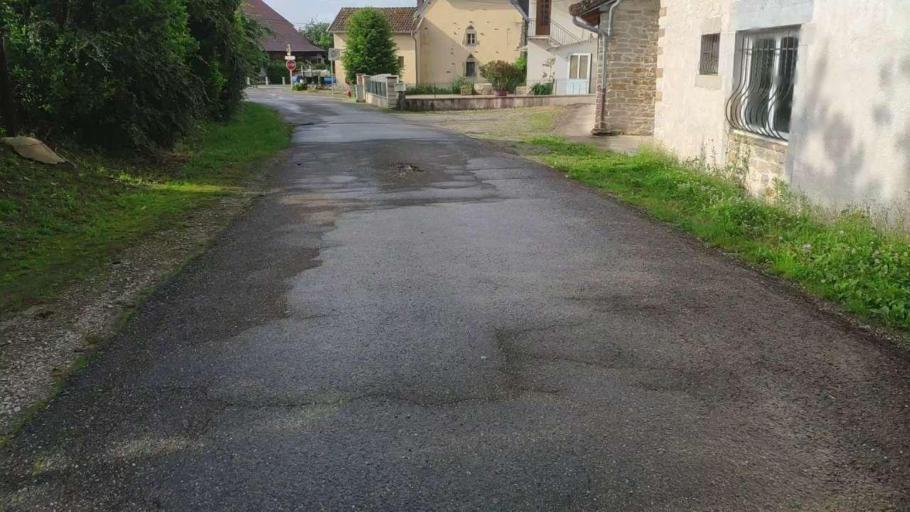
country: FR
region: Franche-Comte
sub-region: Departement du Jura
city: Mont-sous-Vaudrey
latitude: 46.8725
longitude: 5.5223
